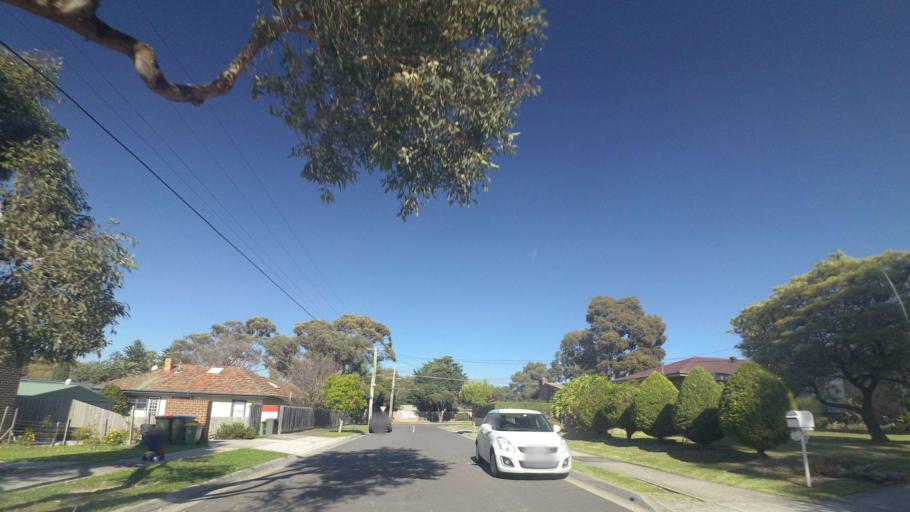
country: AU
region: Victoria
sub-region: Knox
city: Boronia
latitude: -37.8792
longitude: 145.2834
